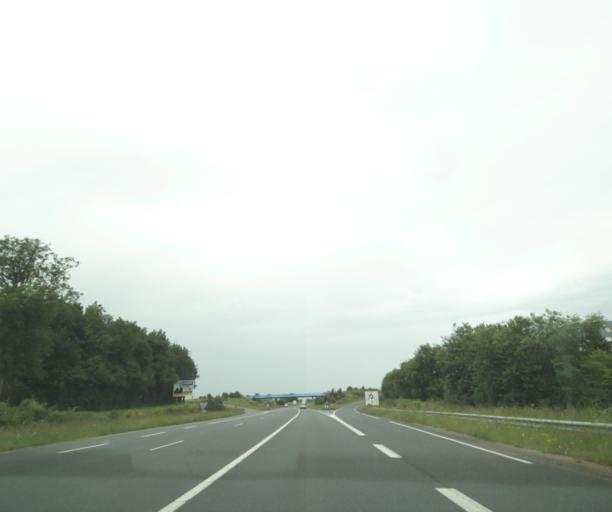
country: FR
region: Poitou-Charentes
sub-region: Departement des Deux-Sevres
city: Saint-Pardoux
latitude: 46.5435
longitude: -0.3128
